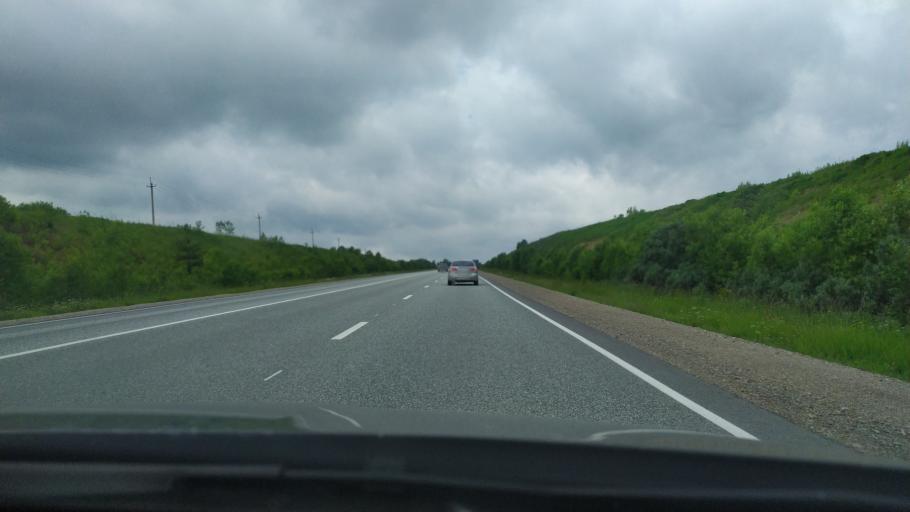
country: RU
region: Perm
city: Verkhnechusovskiye Gorodki
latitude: 58.2652
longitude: 57.3280
